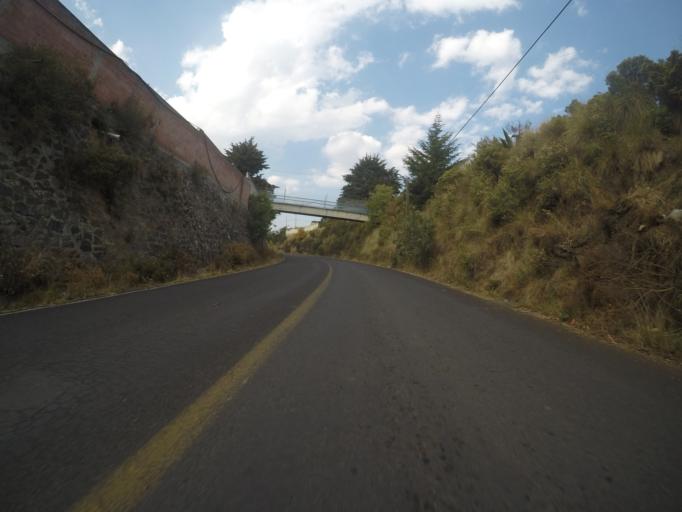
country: MX
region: Mexico
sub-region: Xalatlaco
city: El Aguila (La Mesa)
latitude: 19.1582
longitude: -99.3969
